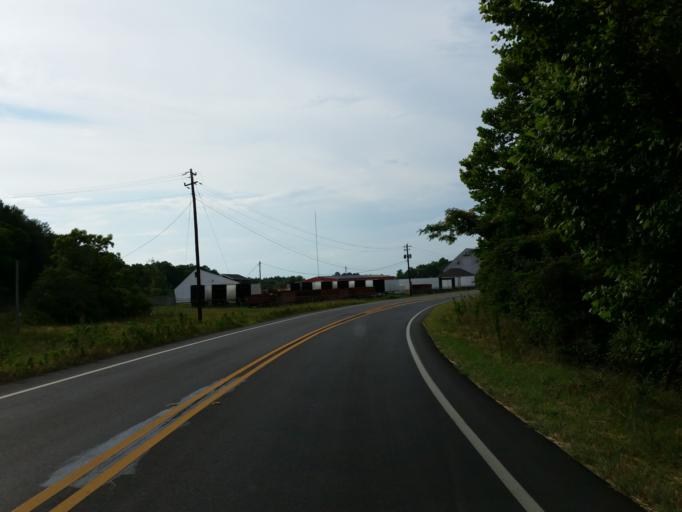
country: US
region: Georgia
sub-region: Turner County
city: Ashburn
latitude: 31.7210
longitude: -83.6638
